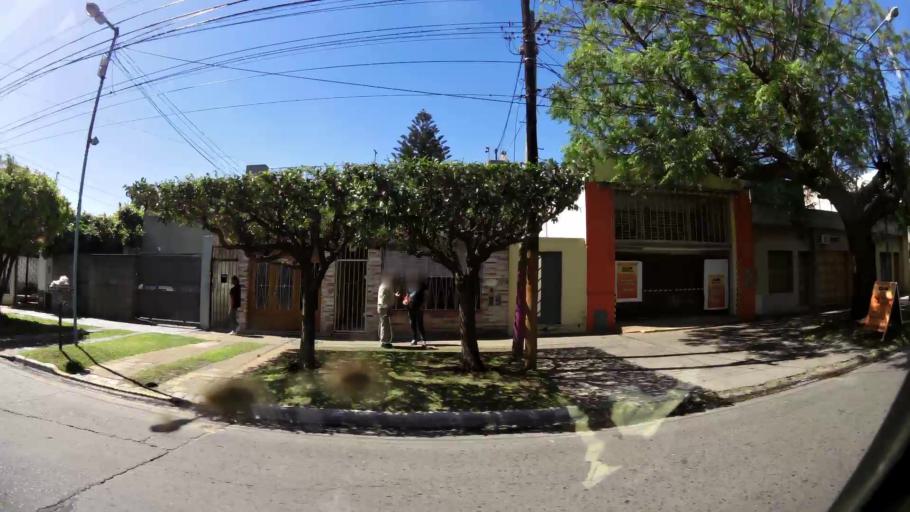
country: AR
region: Buenos Aires
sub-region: Partido de Quilmes
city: Quilmes
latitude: -34.7149
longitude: -58.3031
